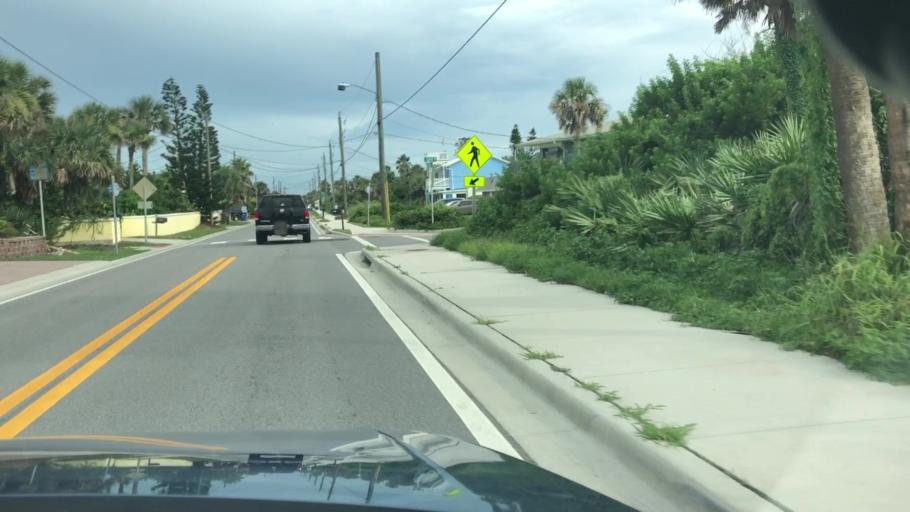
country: US
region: Florida
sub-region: Volusia County
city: Ponce Inlet
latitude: 29.1302
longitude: -80.9570
